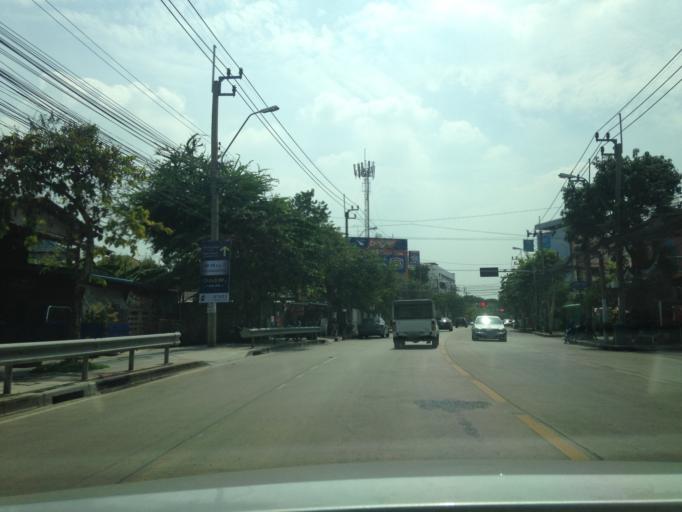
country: TH
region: Bangkok
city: Khan Na Yao
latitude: 13.8349
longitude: 100.6377
